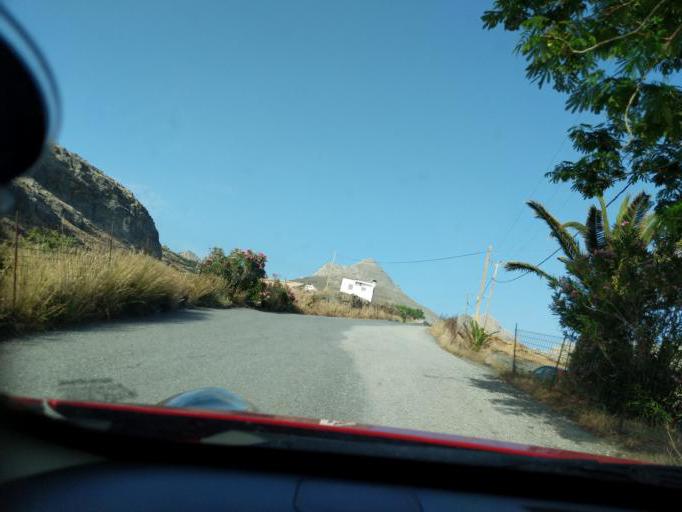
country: GR
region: Crete
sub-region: Nomos Rethymnis
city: Atsipopoulon
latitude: 35.1666
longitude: 24.4227
